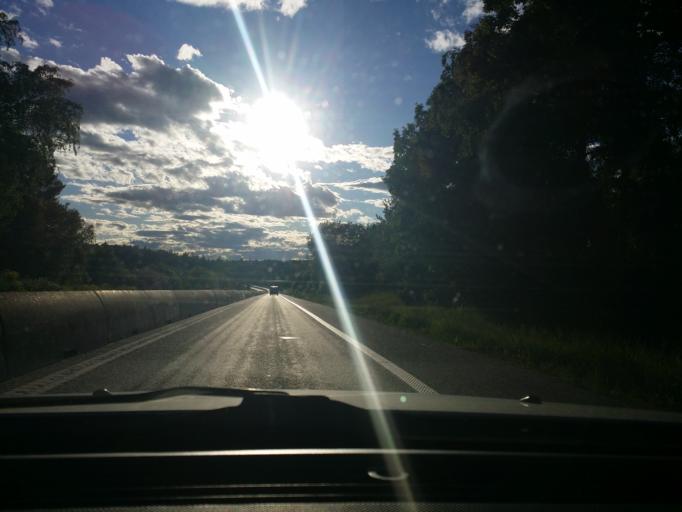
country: SE
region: Stockholm
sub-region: Upplands Vasby Kommun
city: Upplands Vaesby
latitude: 59.4726
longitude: 17.8992
